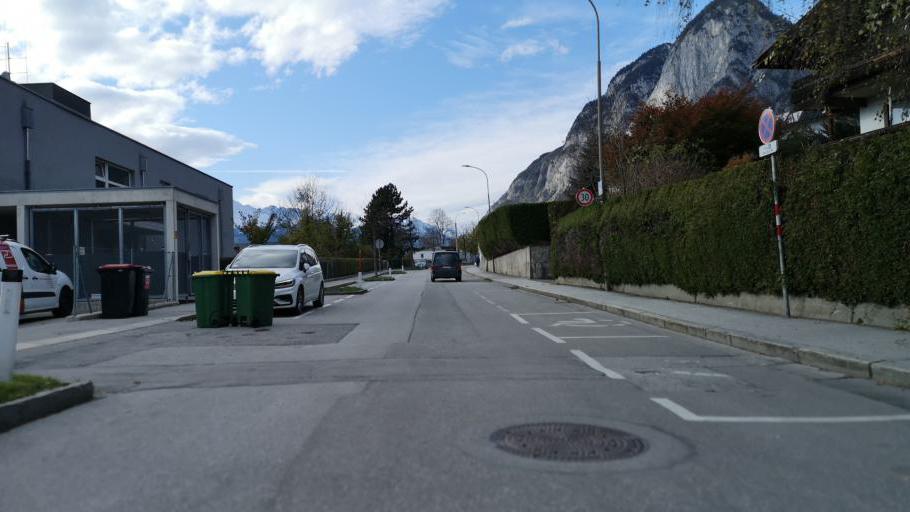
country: AT
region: Tyrol
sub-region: Politischer Bezirk Innsbruck Land
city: Vols
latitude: 47.2671
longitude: 11.3534
